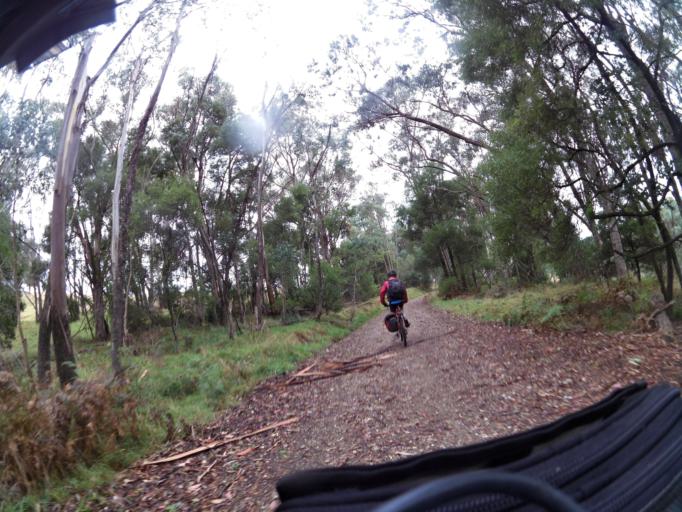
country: AU
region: New South Wales
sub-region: Greater Hume Shire
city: Holbrook
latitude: -36.1562
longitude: 147.4854
